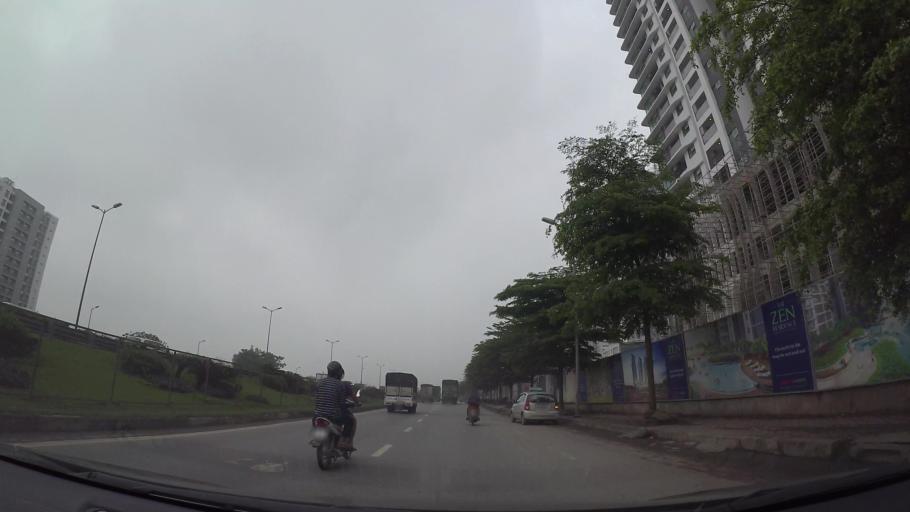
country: VN
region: Ha Noi
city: Van Dien
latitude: 20.9713
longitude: 105.8800
